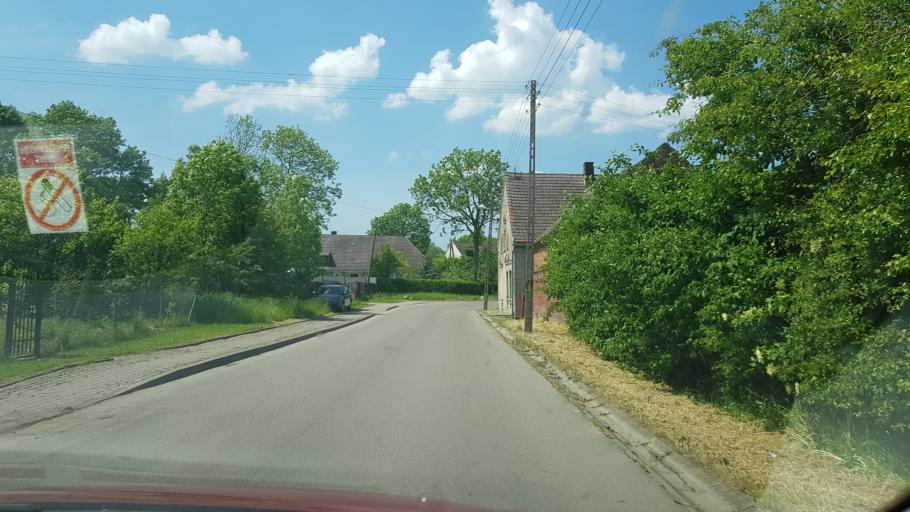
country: PL
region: West Pomeranian Voivodeship
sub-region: Powiat gryficki
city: Trzebiatow
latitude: 54.0833
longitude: 15.2149
